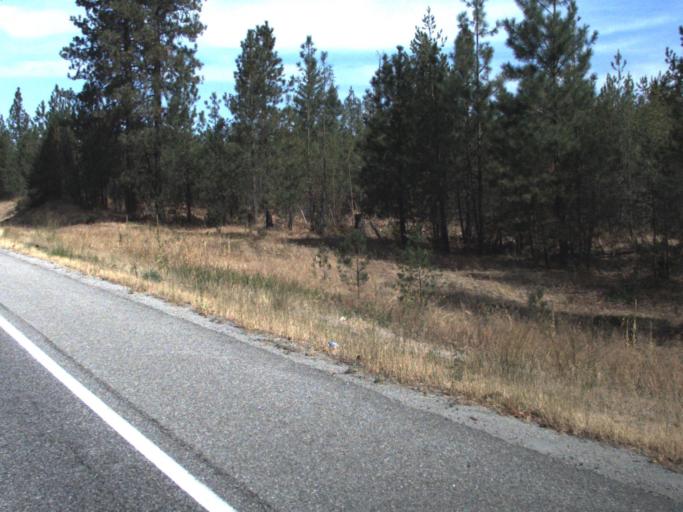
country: US
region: Washington
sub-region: Stevens County
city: Chewelah
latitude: 48.0878
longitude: -117.6337
